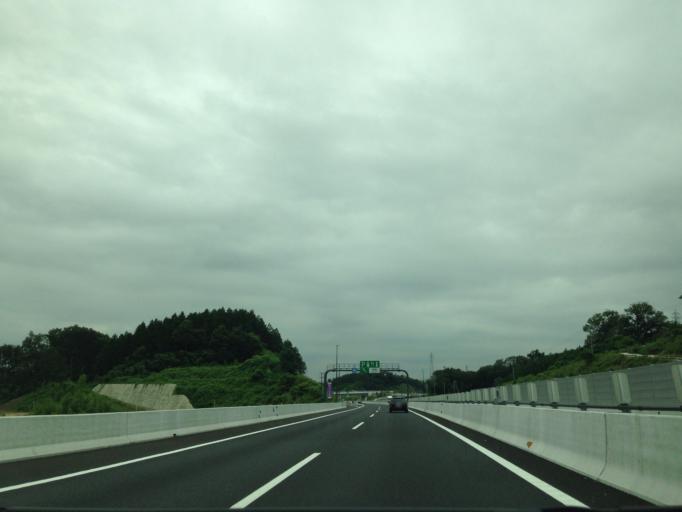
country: JP
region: Aichi
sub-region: Toyota-shi
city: Toyota
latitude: 35.0271
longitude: 137.2240
